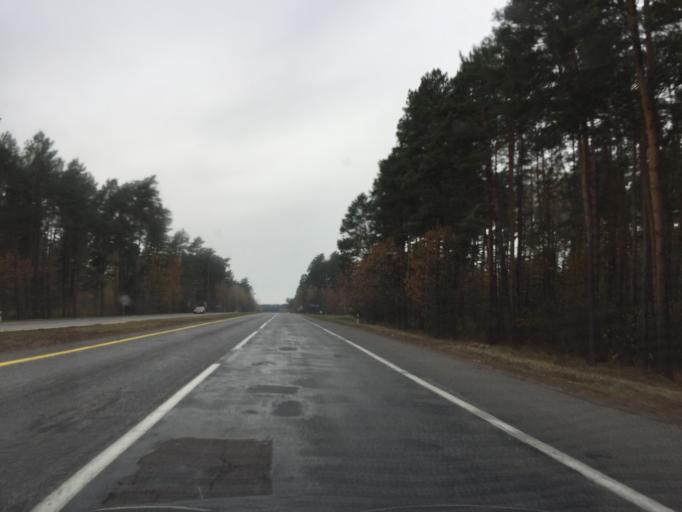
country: BY
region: Gomel
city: Horad Rechytsa
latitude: 52.3589
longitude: 30.6677
